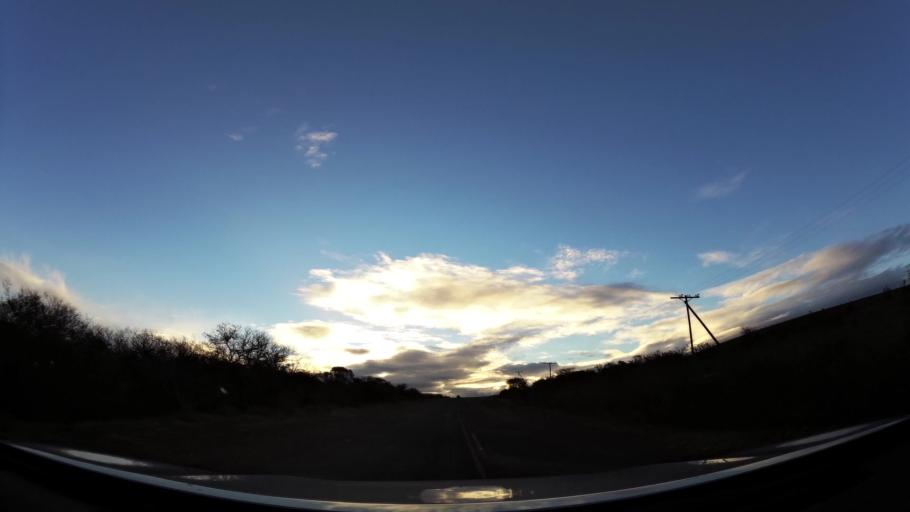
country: ZA
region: Western Cape
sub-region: Eden District Municipality
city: Riversdale
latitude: -34.0719
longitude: 20.9052
